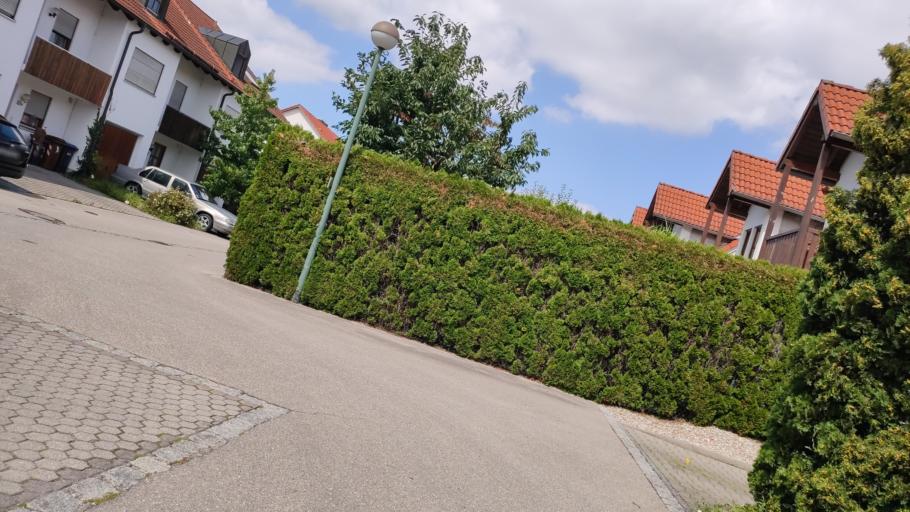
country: DE
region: Bavaria
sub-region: Swabia
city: Konigsbrunn
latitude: 48.2677
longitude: 10.9014
